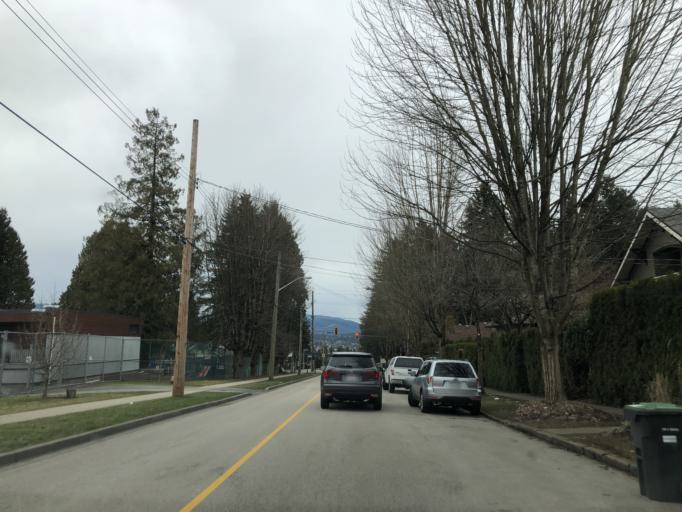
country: CA
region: British Columbia
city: New Westminster
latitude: 49.2169
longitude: -122.9134
